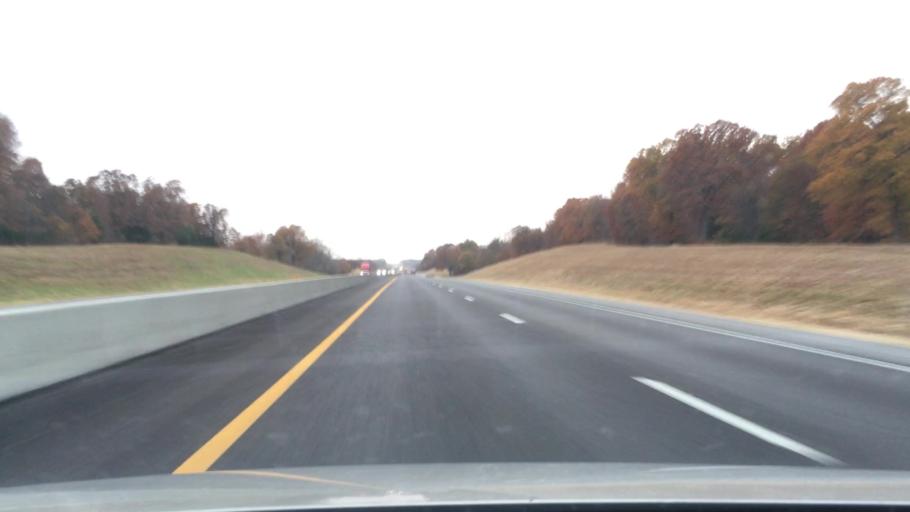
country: US
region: Oklahoma
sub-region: Lincoln County
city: Stroud
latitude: 35.7430
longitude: -96.7462
